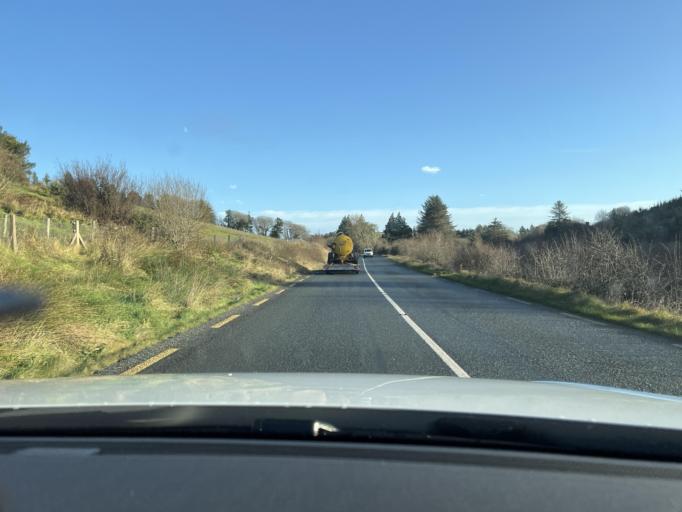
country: IE
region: Connaught
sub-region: County Leitrim
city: Manorhamilton
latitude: 54.1988
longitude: -8.1892
